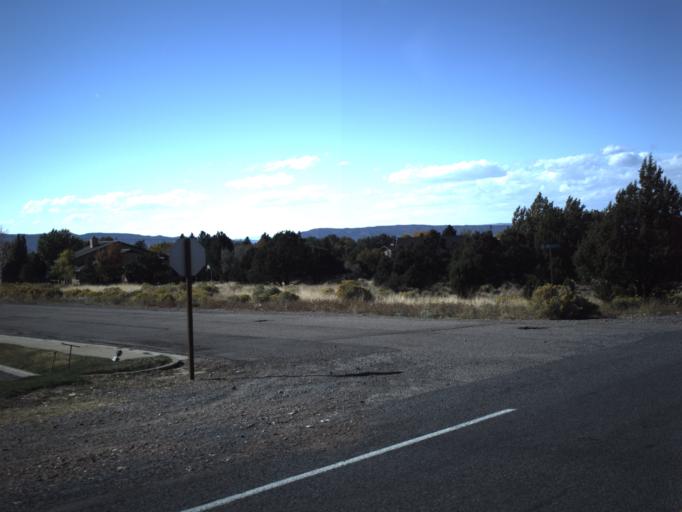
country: US
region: Utah
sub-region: Iron County
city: Parowan
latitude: 37.8375
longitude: -112.8193
